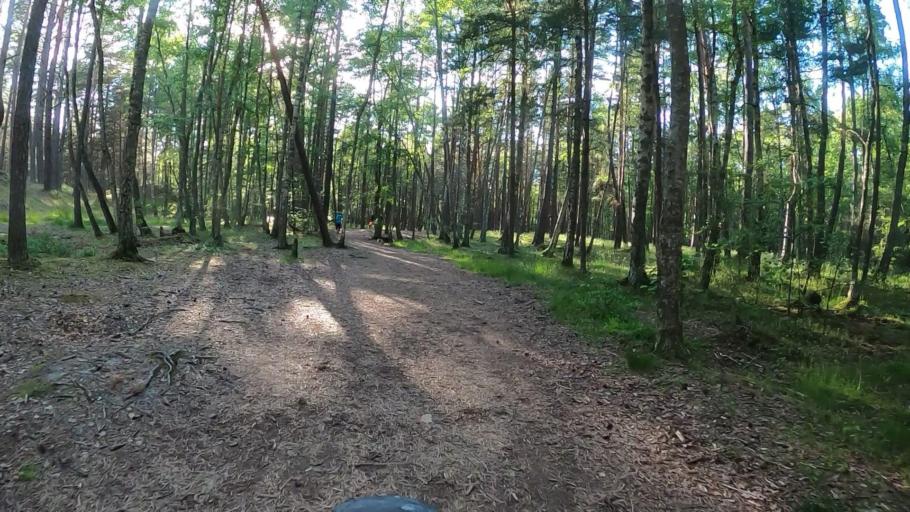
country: LV
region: Carnikava
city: Carnikava
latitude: 57.1386
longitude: 24.2432
